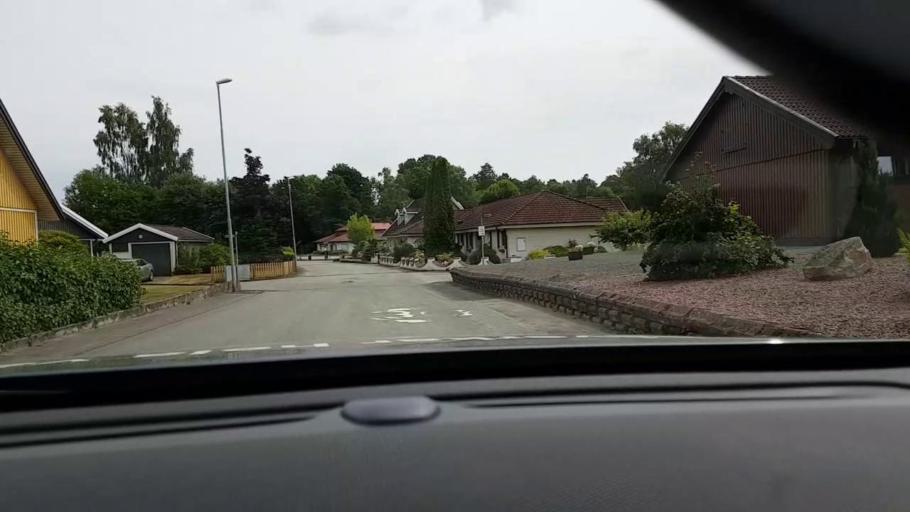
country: SE
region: Skane
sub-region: Hassleholms Kommun
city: Hassleholm
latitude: 56.1676
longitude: 13.7382
